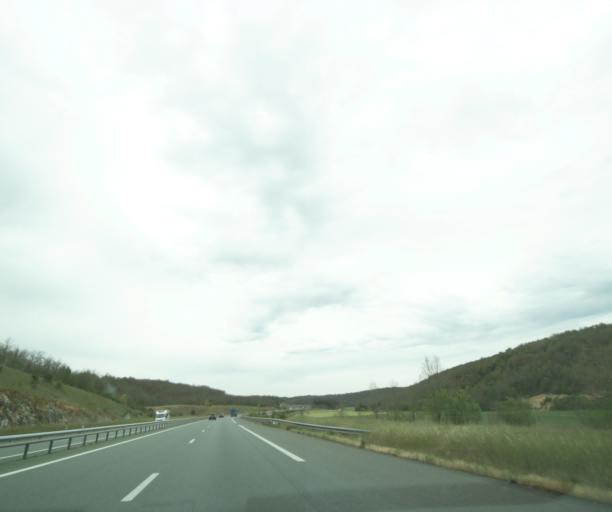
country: FR
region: Midi-Pyrenees
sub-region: Departement du Lot
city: Le Vigan
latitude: 44.7779
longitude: 1.5339
